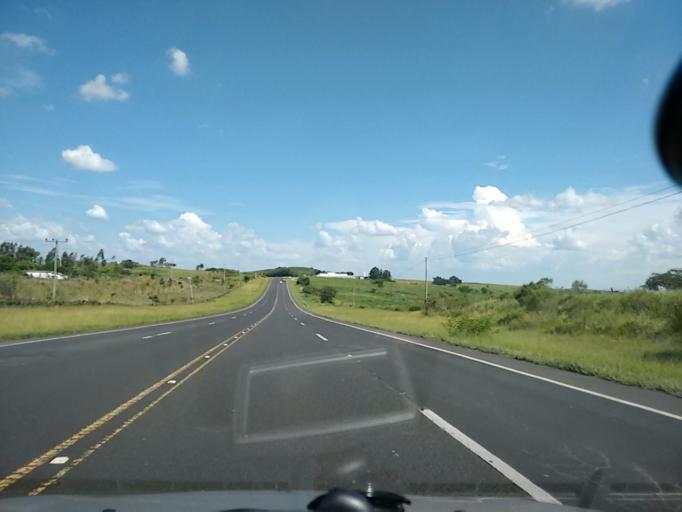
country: BR
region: Sao Paulo
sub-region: Pompeia
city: Pompeia
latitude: -22.0856
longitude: -50.2784
